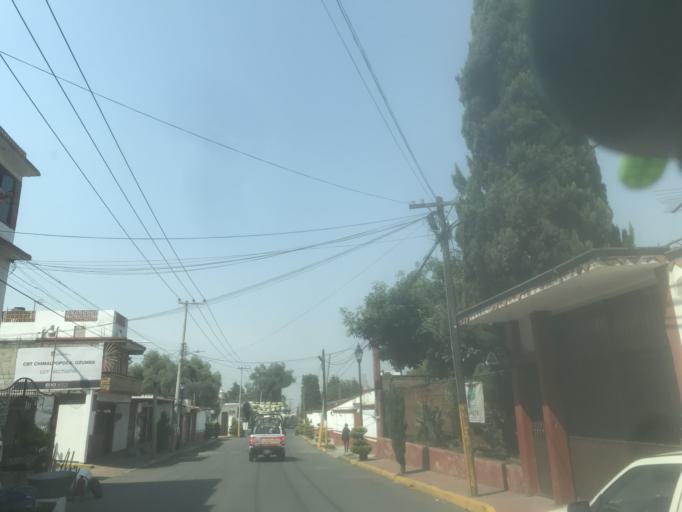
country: MX
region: Mexico
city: Ozumba de Alzate
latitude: 19.0296
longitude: -98.8008
